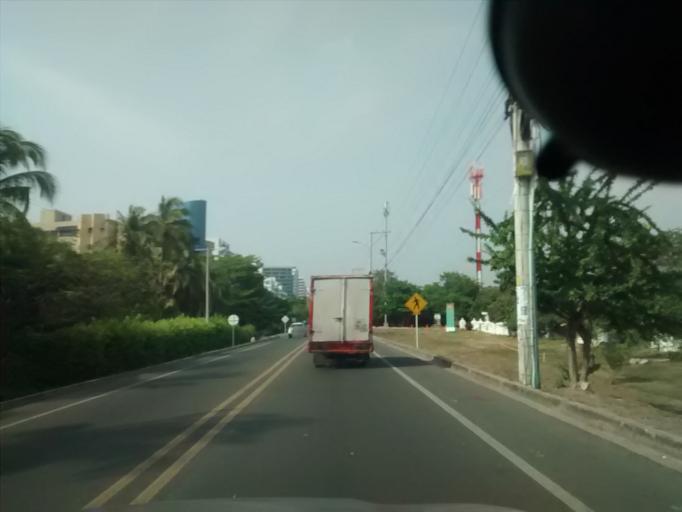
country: CO
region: Bolivar
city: Cartagena
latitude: 10.4599
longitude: -75.5058
